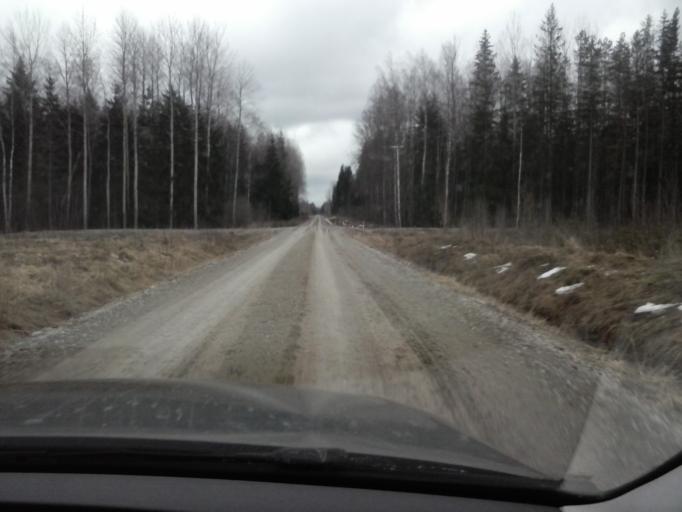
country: EE
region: Jogevamaa
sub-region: Mustvee linn
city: Mustvee
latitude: 59.0589
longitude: 26.8251
